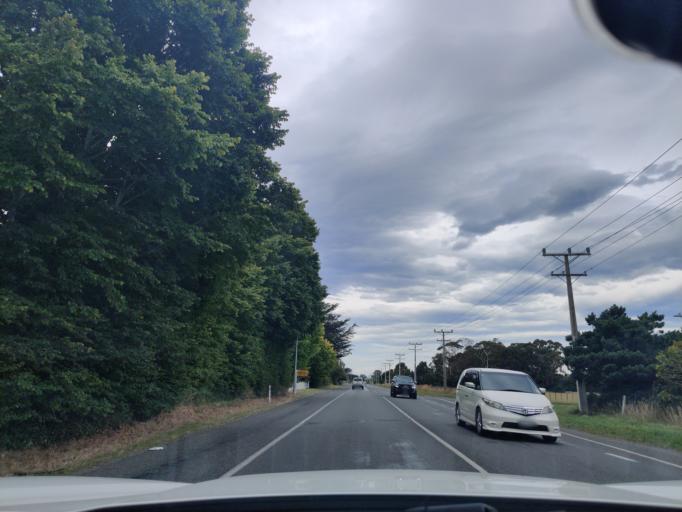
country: NZ
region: Wellington
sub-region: Masterton District
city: Masterton
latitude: -41.0130
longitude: 175.5407
